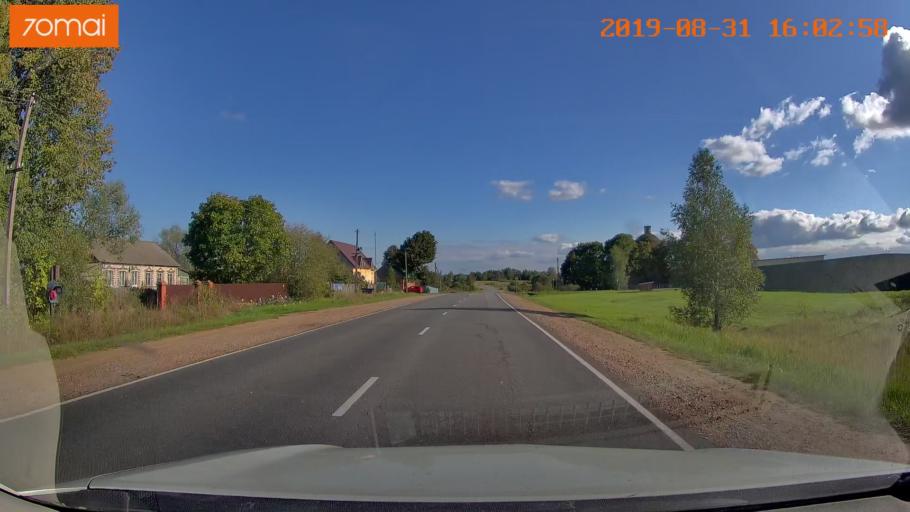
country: RU
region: Kaluga
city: Yukhnov
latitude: 54.6695
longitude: 35.3087
